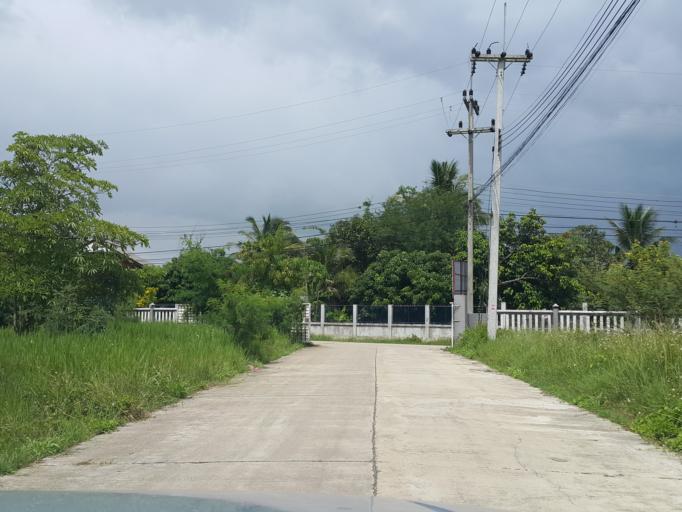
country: TH
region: Chiang Mai
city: San Kamphaeng
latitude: 18.7876
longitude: 99.1097
